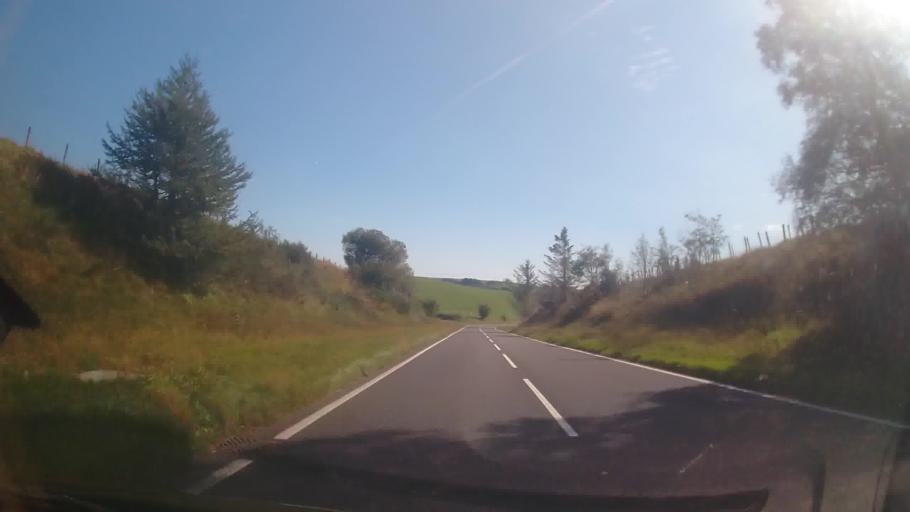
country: GB
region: Wales
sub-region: Sir Powys
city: Mochdre
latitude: 52.4423
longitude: -3.3474
